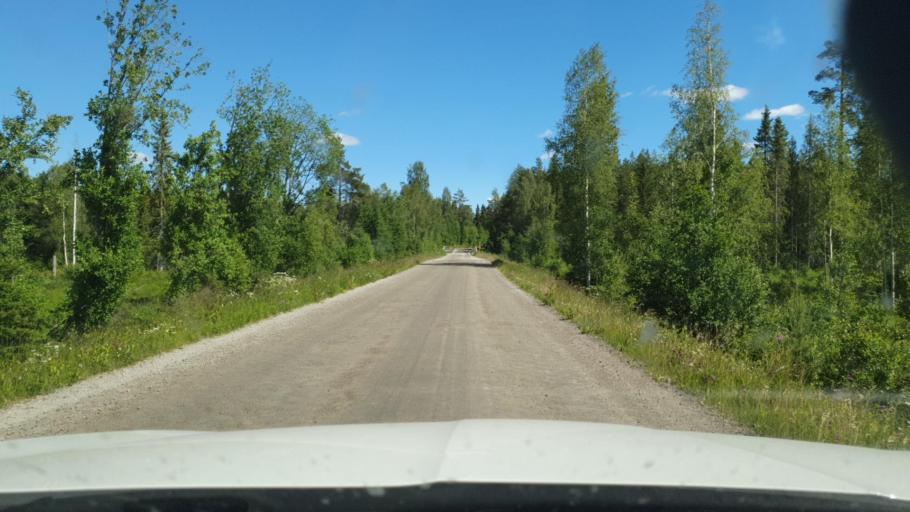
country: SE
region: Vaesterbotten
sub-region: Skelleftea Kommun
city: Byske
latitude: 65.1052
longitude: 21.1759
